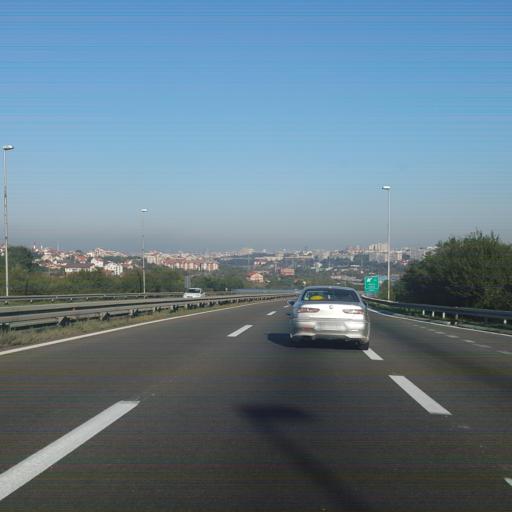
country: RS
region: Central Serbia
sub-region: Belgrade
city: Zvezdara
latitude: 44.7651
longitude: 20.5266
